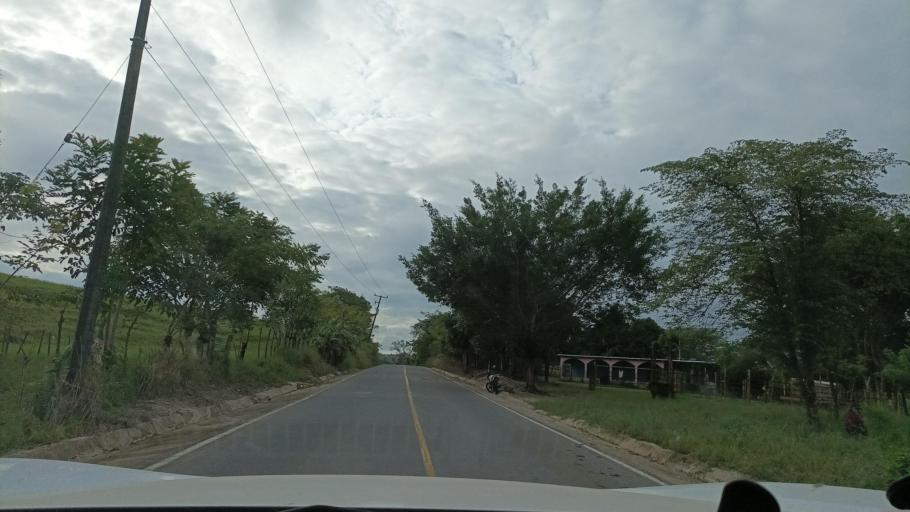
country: MX
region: Veracruz
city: Hidalgotitlan
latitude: 17.7459
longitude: -94.4927
